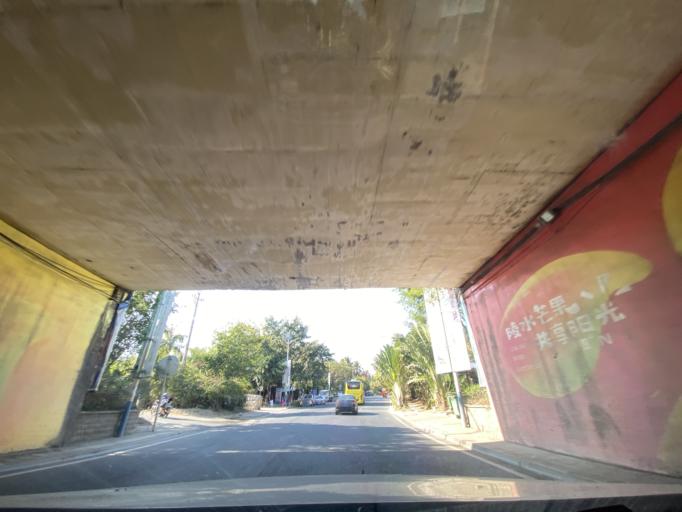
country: CN
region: Hainan
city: Yingzhou
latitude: 18.4372
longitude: 109.8499
